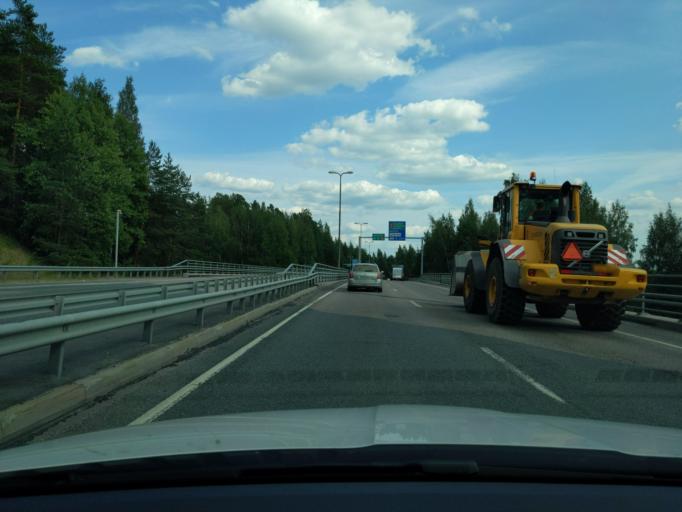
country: FI
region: Paijanne Tavastia
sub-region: Lahti
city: Lahti
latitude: 60.9724
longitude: 25.7063
